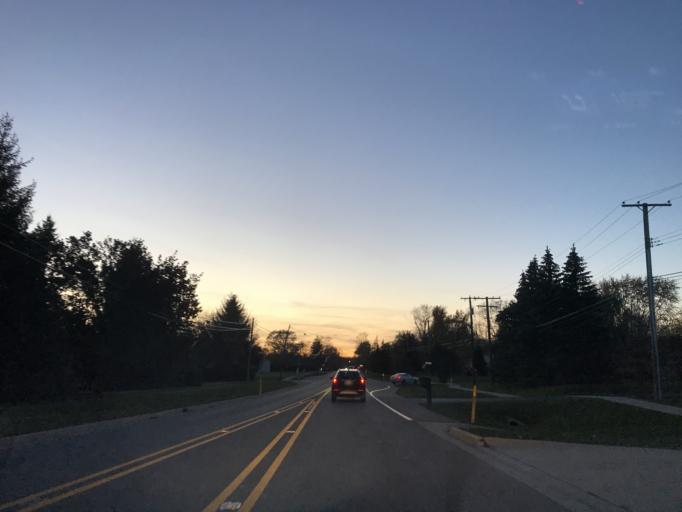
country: US
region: Michigan
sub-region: Oakland County
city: Farmington
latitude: 42.4699
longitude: -83.3677
